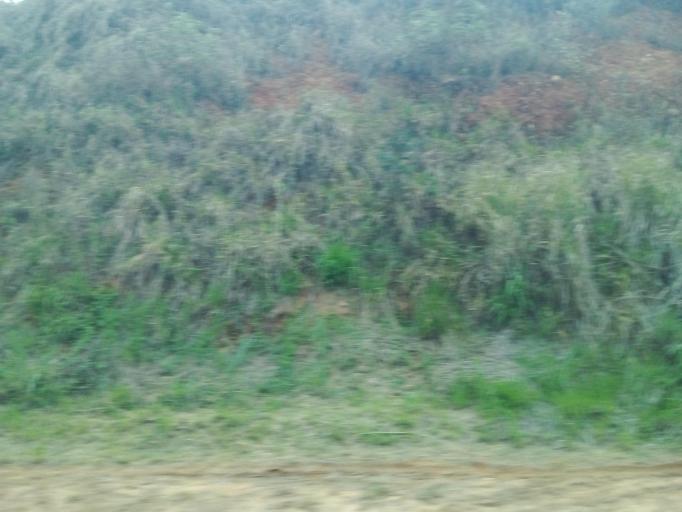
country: BR
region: Minas Gerais
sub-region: Nova Era
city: Nova Era
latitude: -19.7502
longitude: -43.0227
